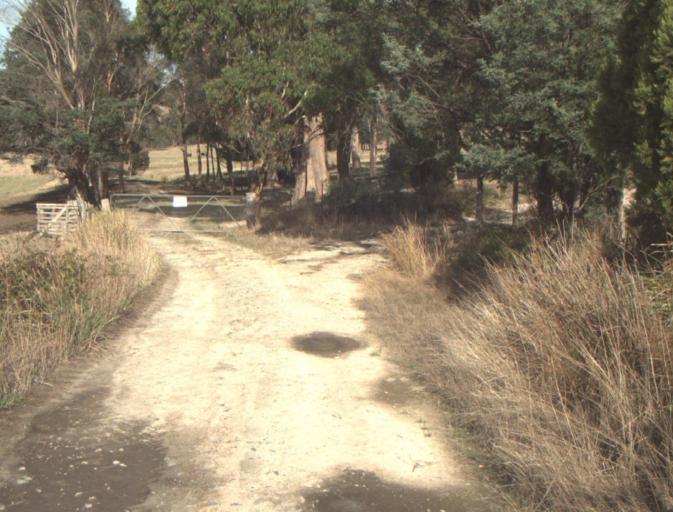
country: AU
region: Tasmania
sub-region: Launceston
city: Mayfield
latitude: -41.2214
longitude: 147.1580
